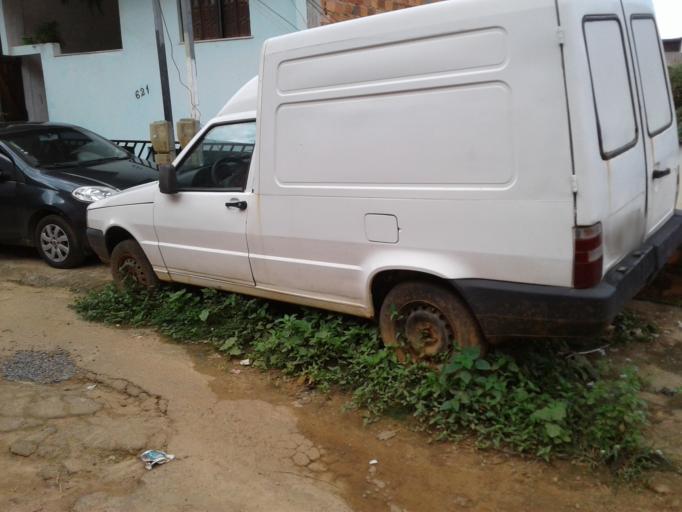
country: BR
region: Bahia
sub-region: Salvador
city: Salvador
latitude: -12.9110
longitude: -38.4742
